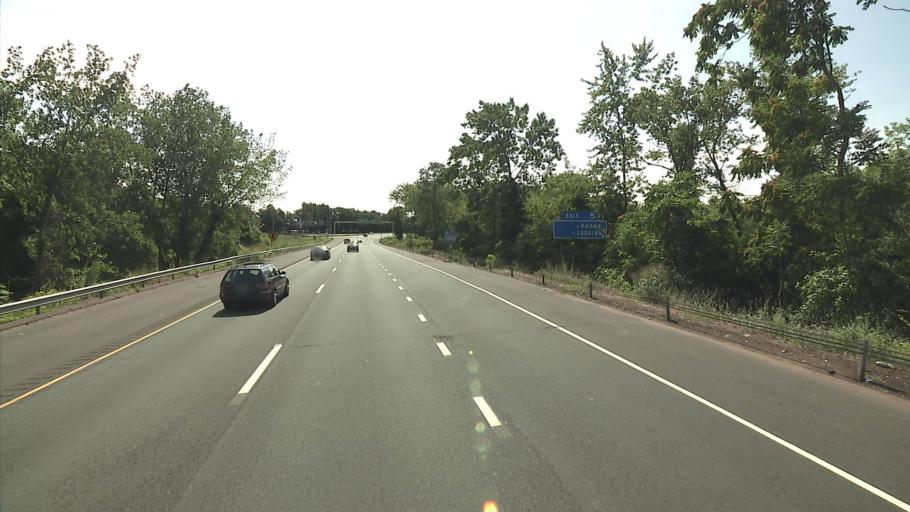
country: US
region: Connecticut
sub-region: Hartford County
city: Hartford
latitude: 41.7536
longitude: -72.6477
